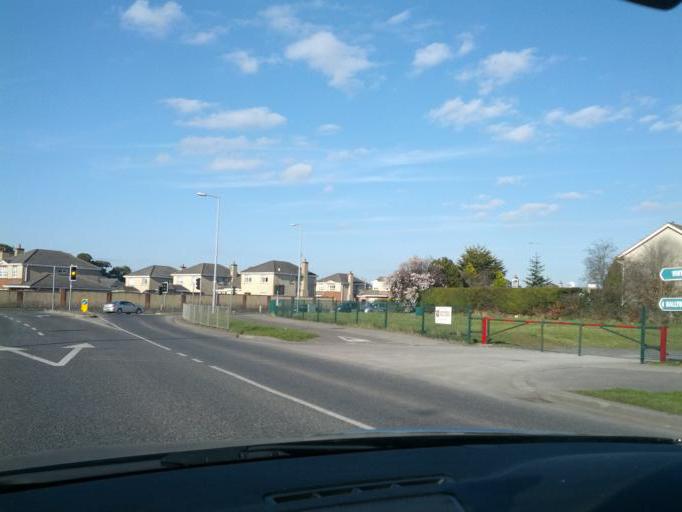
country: IE
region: Leinster
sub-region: Kildare
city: Naas
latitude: 53.2136
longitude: -6.6811
